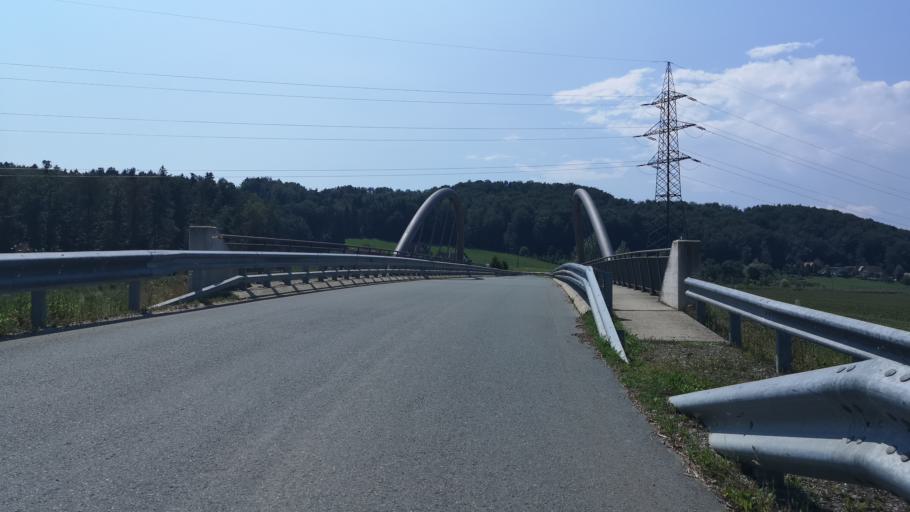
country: AT
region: Styria
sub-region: Politischer Bezirk Deutschlandsberg
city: Gross Sankt Florian
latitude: 46.8153
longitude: 15.2879
